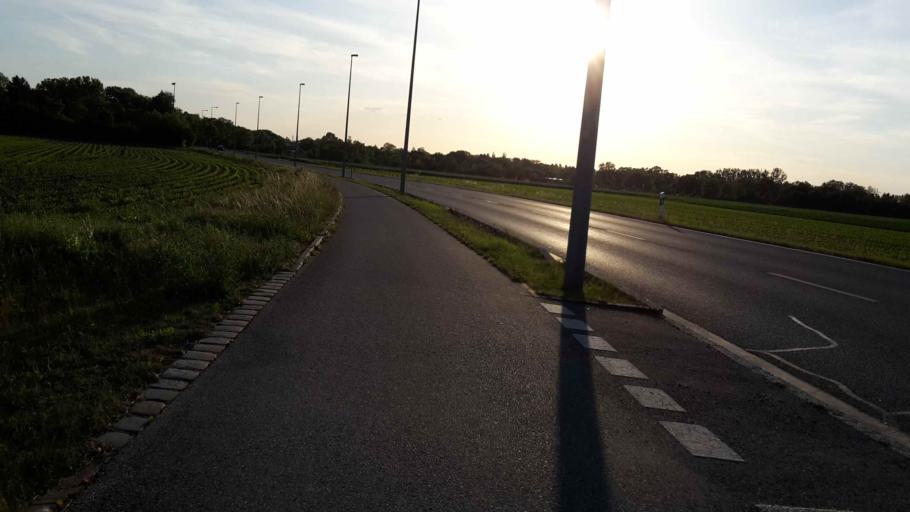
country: DE
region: Bavaria
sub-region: Upper Bavaria
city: Karlsfeld
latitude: 48.2173
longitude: 11.4965
